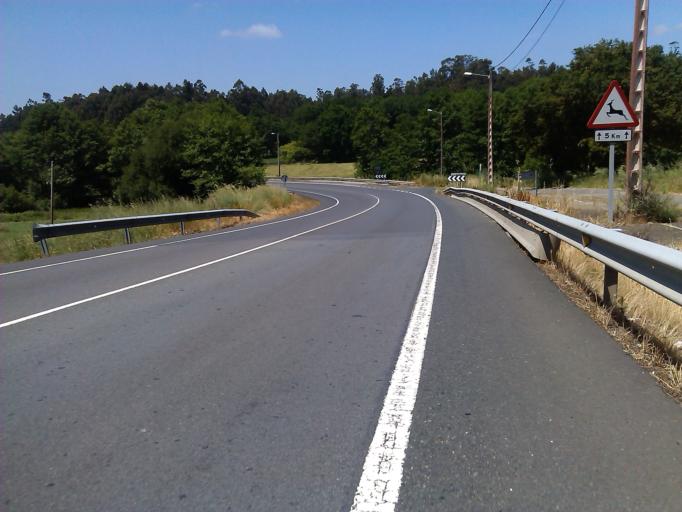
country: ES
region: Galicia
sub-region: Provincia da Coruna
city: Touro
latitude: 42.9038
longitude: -8.3698
